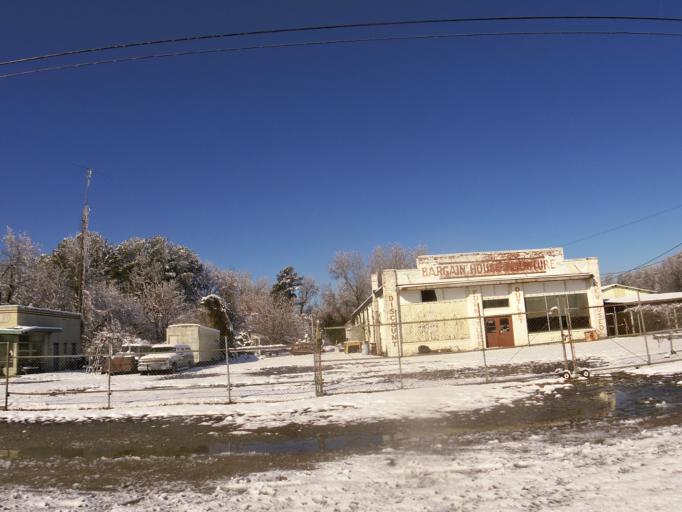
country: US
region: North Carolina
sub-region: Nash County
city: Sharpsburg
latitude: 35.9020
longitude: -77.8140
